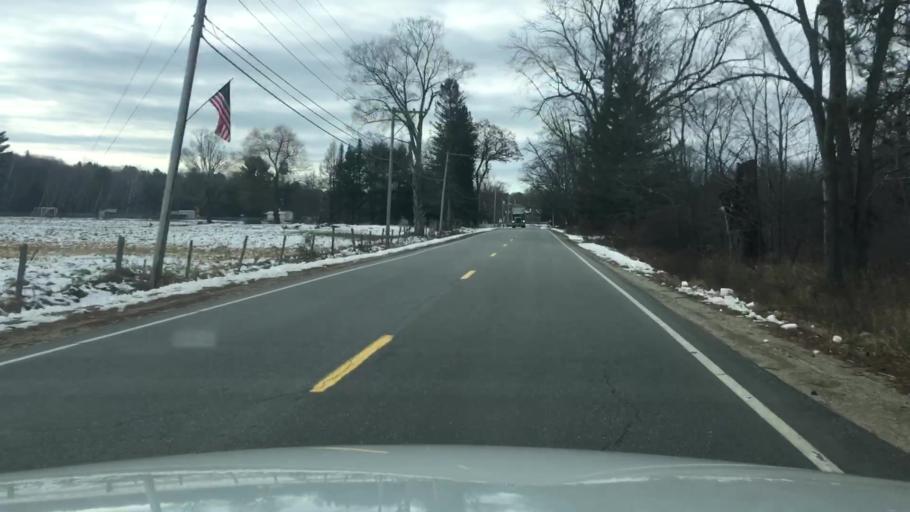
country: US
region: Maine
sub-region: Oxford County
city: Canton
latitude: 44.4446
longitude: -70.3110
